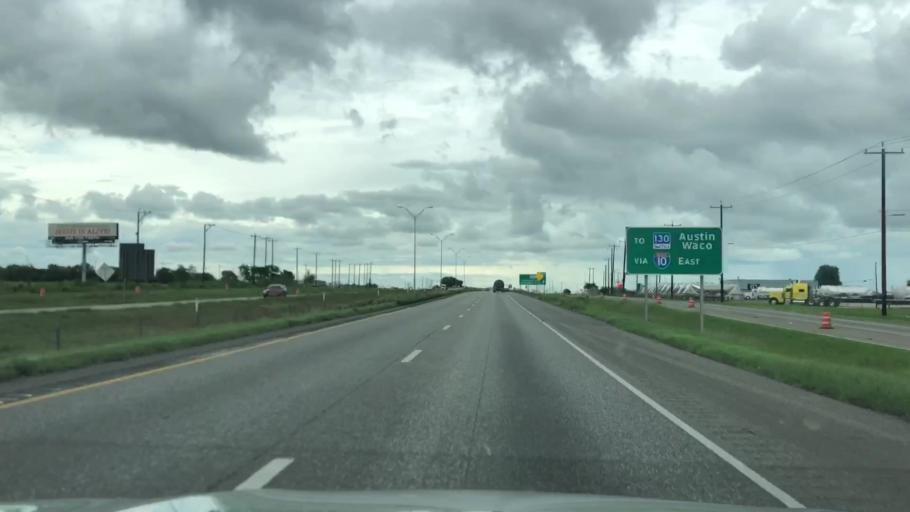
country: US
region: Texas
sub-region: Bexar County
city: Converse
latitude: 29.4632
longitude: -98.2982
